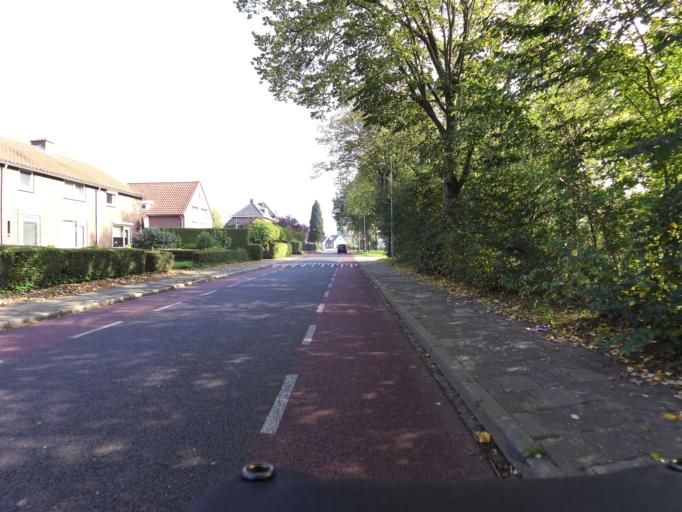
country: NL
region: Gelderland
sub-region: Gemeente Zevenaar
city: Zevenaar
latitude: 51.8607
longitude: 6.0510
